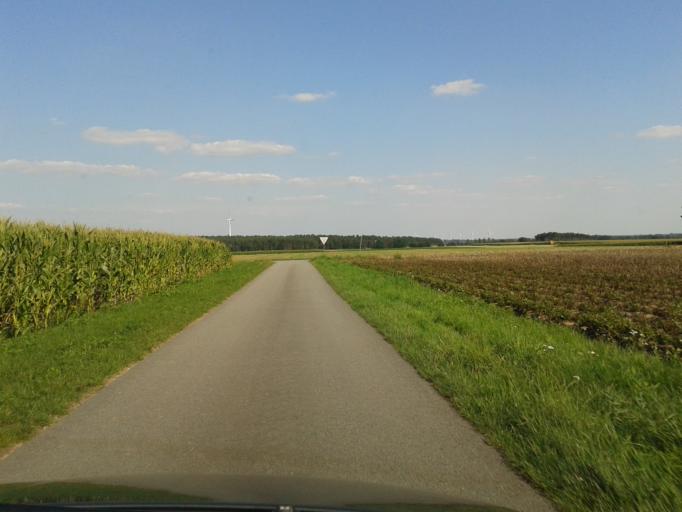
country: DE
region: Lower Saxony
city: Woltersdorf
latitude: 52.9264
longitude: 11.2266
